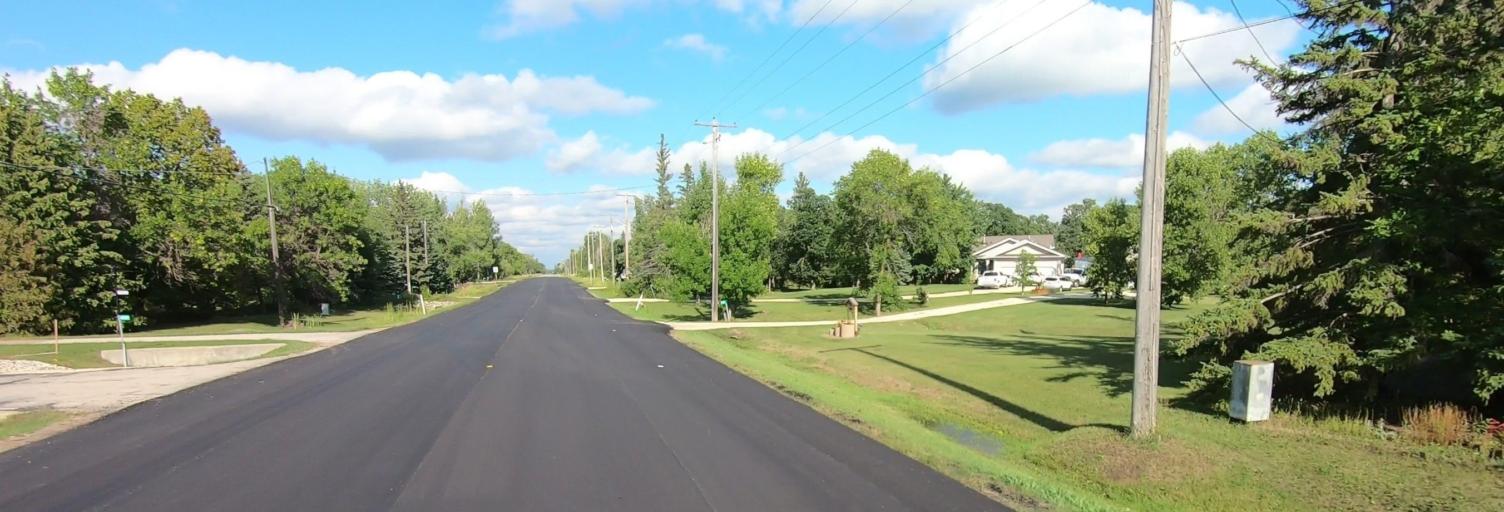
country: CA
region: Manitoba
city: Selkirk
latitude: 50.0327
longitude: -97.0014
